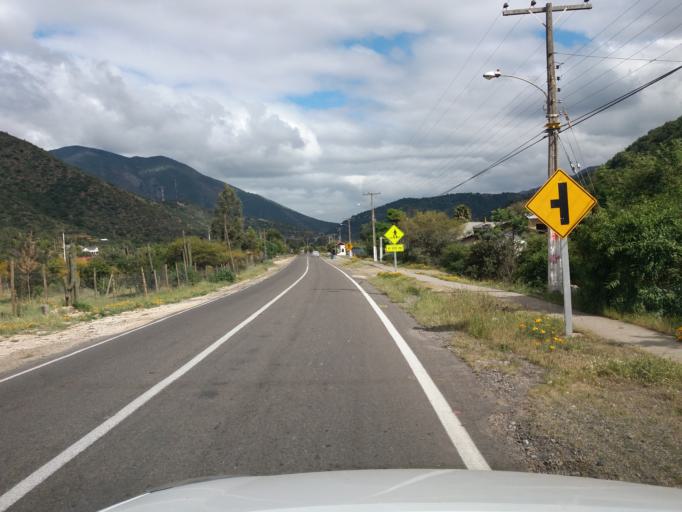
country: CL
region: Valparaiso
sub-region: Provincia de Marga Marga
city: Limache
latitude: -33.0579
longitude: -71.0835
